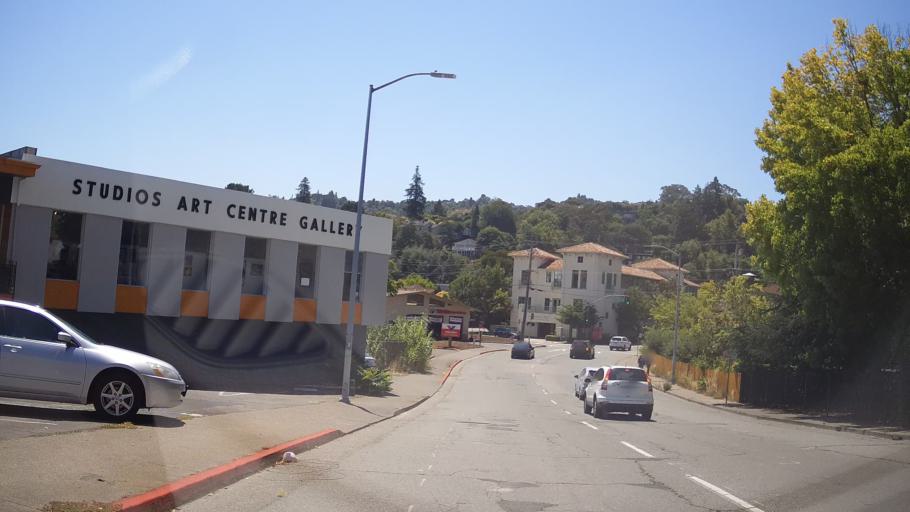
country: US
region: California
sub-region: Marin County
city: San Rafael
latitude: 37.9725
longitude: -122.5338
